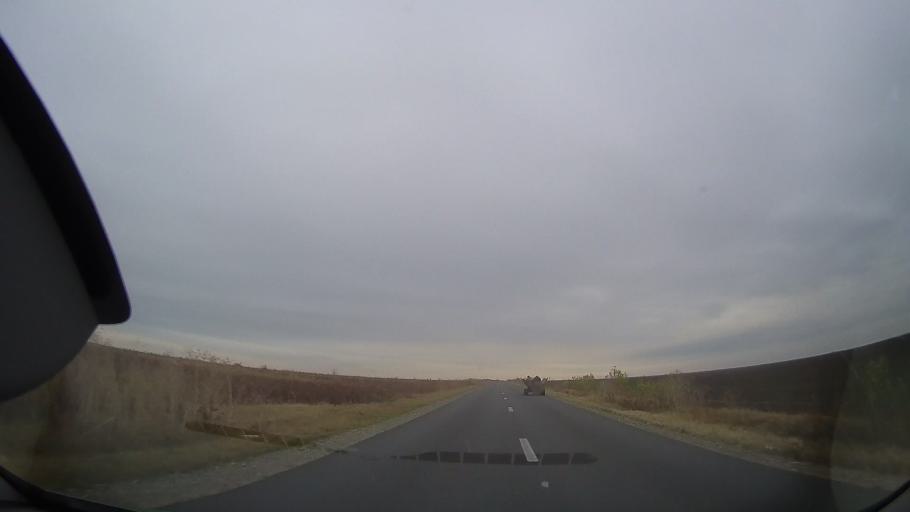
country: RO
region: Ialomita
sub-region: Oras Amara
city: Amara
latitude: 44.6409
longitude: 27.3007
